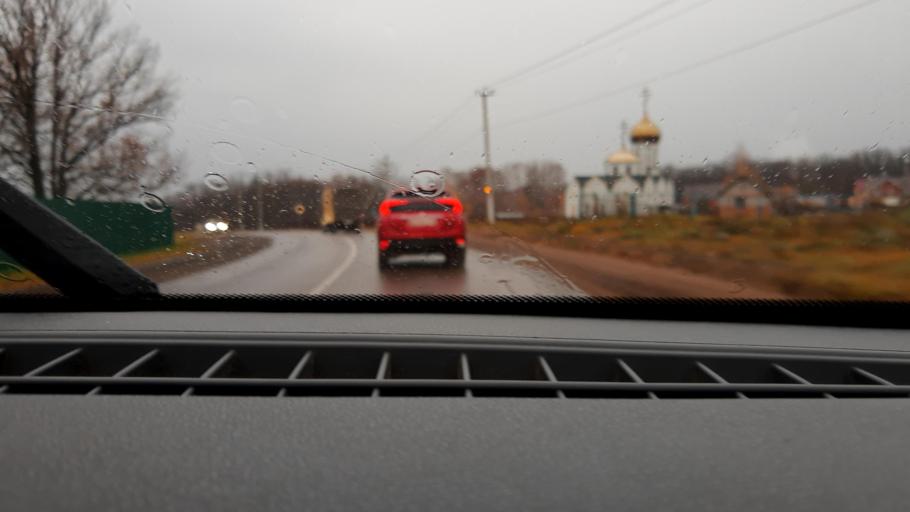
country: RU
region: Bashkortostan
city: Mikhaylovka
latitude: 54.8135
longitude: 55.8831
